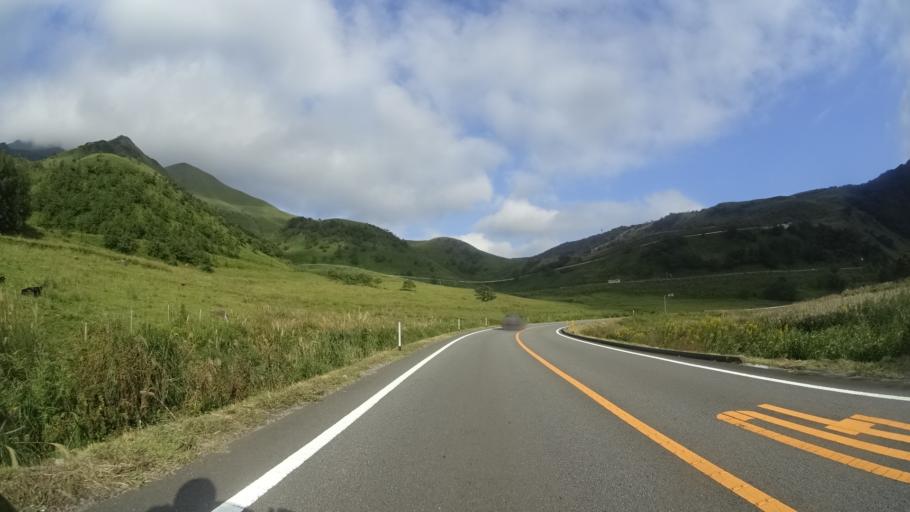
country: JP
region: Oita
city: Beppu
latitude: 33.2631
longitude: 131.3781
